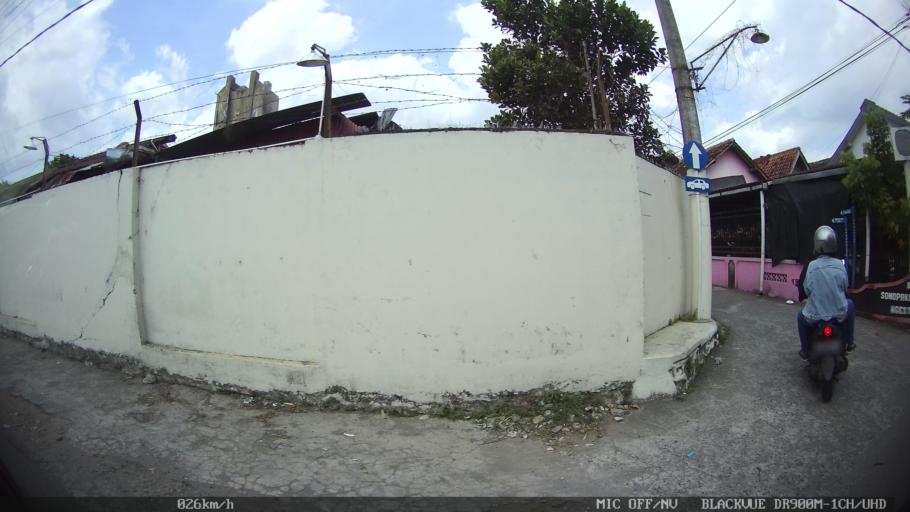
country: ID
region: Daerah Istimewa Yogyakarta
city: Gamping Lor
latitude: -7.8020
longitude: 110.3384
